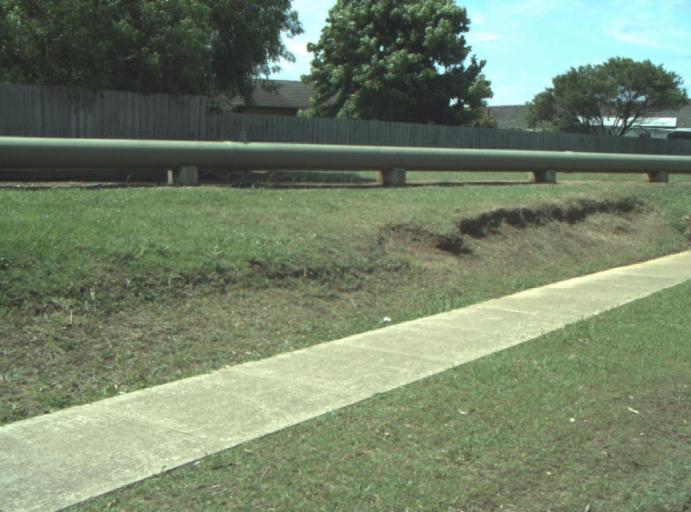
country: AU
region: Victoria
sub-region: Greater Geelong
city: Wandana Heights
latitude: -38.2119
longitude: 144.3333
